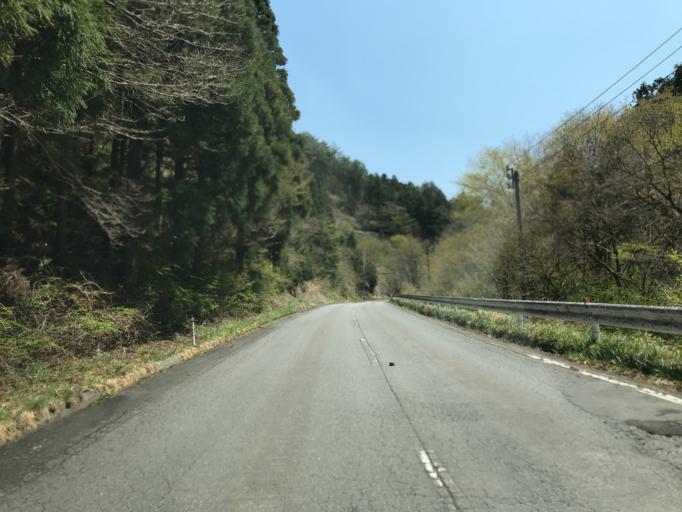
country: JP
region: Ibaraki
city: Kitaibaraki
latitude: 36.9802
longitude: 140.6257
